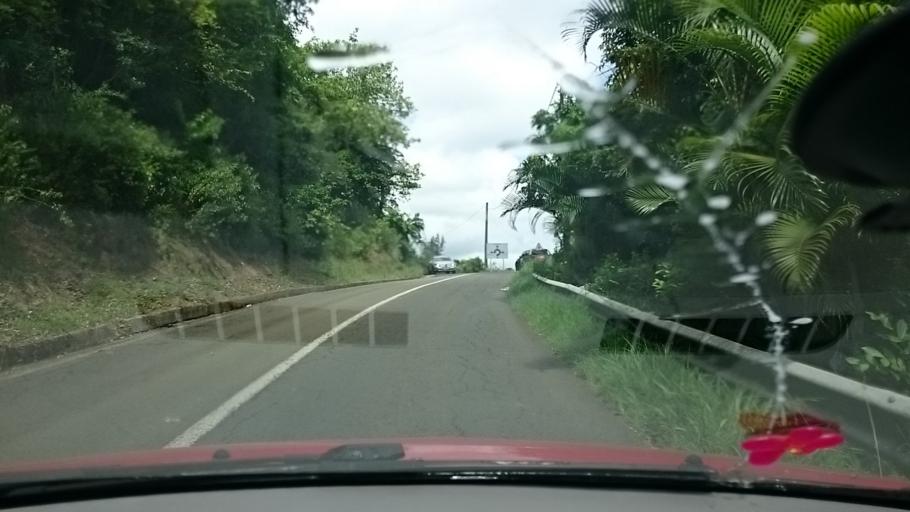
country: MQ
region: Martinique
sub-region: Martinique
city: La Trinite
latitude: 14.7553
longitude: -60.9225
